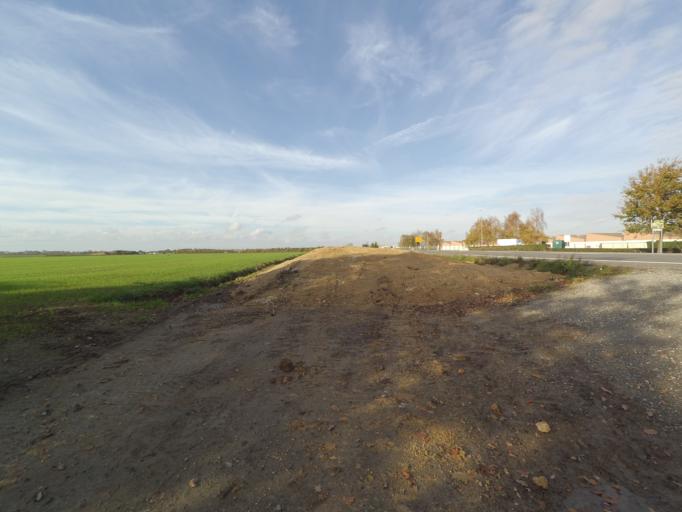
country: FR
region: Pays de la Loire
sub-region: Departement de la Vendee
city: Saint-Hilaire-de-Loulay
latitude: 47.0217
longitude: -1.3464
